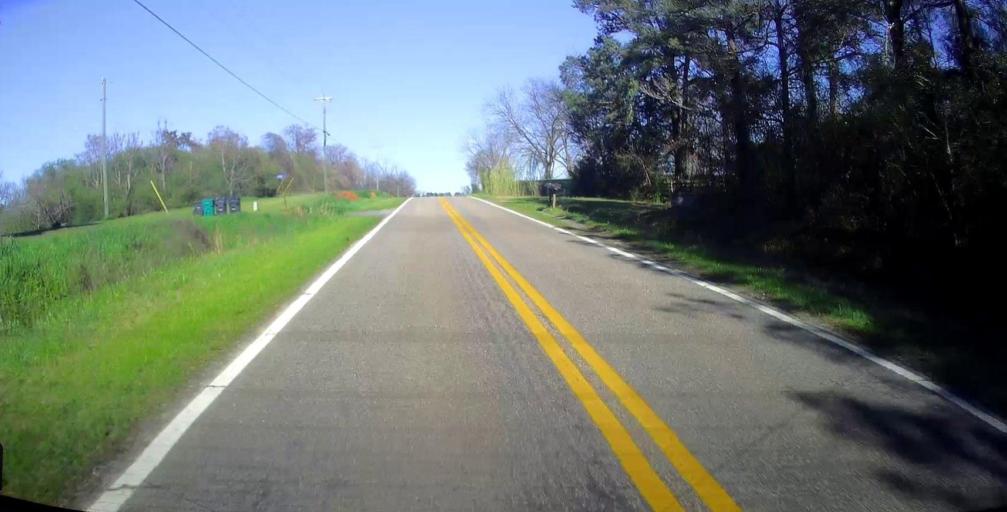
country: US
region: Georgia
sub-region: Peach County
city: Fort Valley
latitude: 32.6538
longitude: -83.8798
